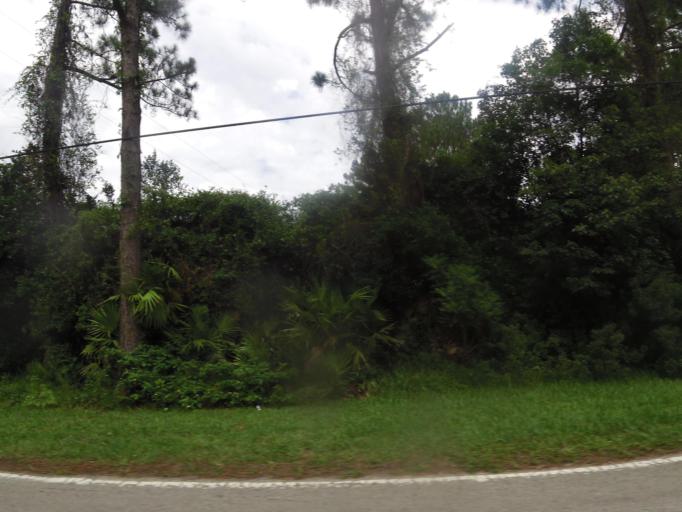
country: US
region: Florida
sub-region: Duval County
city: Jacksonville
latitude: 30.2972
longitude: -81.5298
